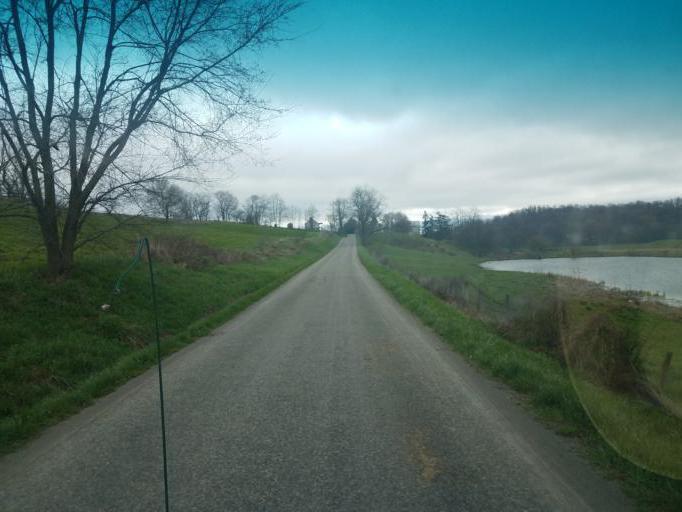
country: US
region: Ohio
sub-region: Stark County
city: Brewster
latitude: 40.6425
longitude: -81.7252
